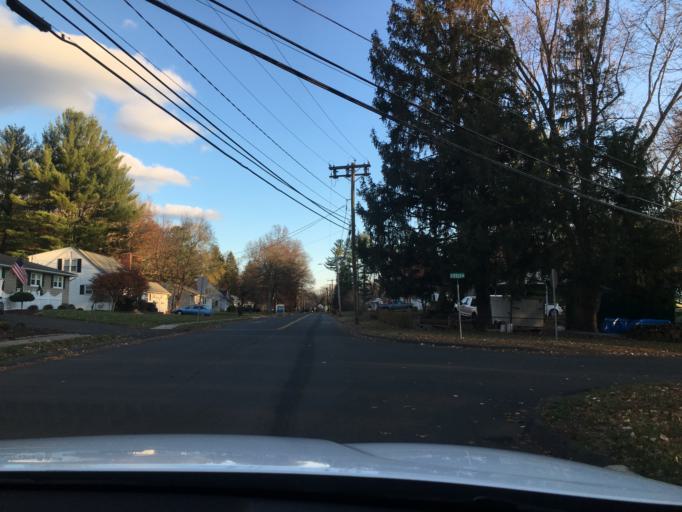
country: US
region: Connecticut
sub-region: Hartford County
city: Southwood Acres
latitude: 41.9600
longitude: -72.5746
